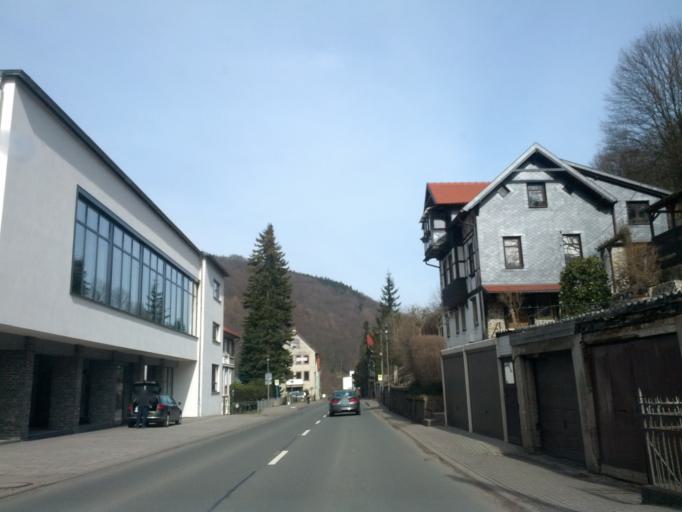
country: DE
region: Thuringia
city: Ruhla
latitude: 50.8988
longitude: 10.3646
